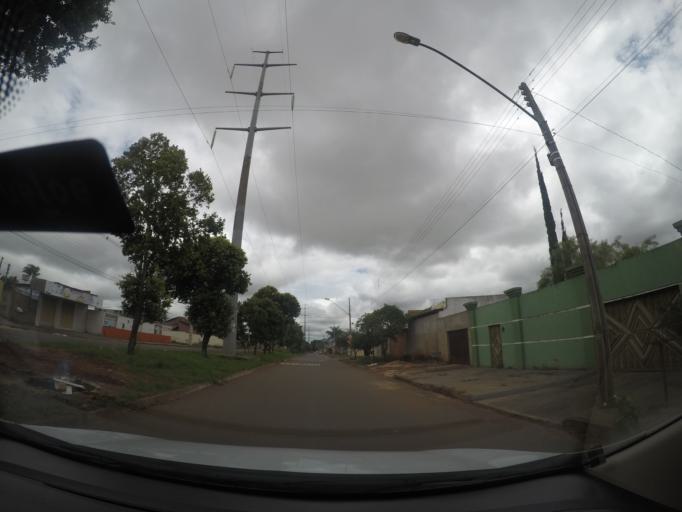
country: BR
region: Goias
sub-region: Goiania
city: Goiania
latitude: -16.7326
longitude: -49.3587
